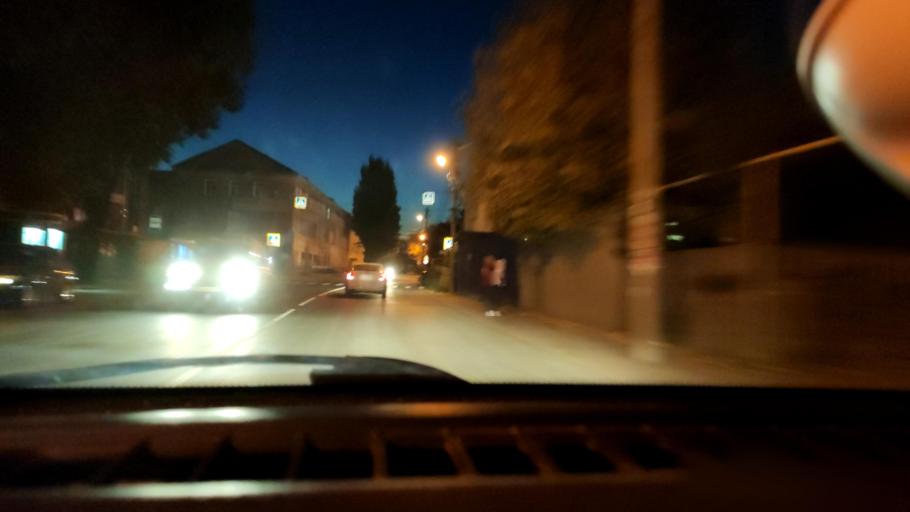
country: RU
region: Samara
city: Samara
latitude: 53.1832
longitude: 50.1225
